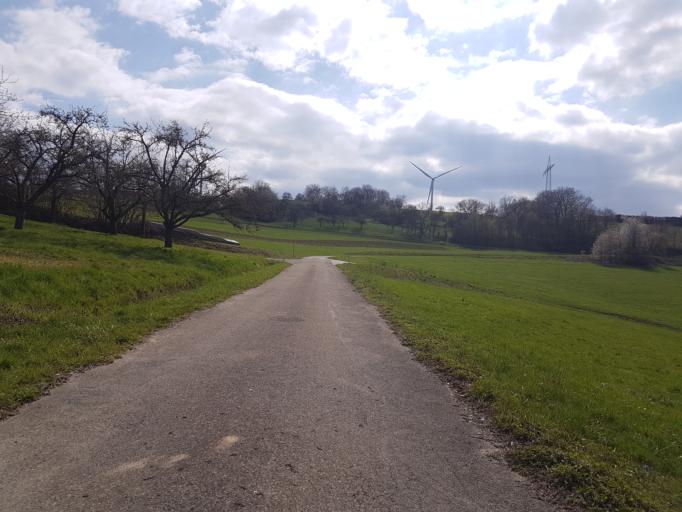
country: DE
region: Baden-Wuerttemberg
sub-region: Regierungsbezirk Stuttgart
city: Weissbach
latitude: 49.3411
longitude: 9.6080
